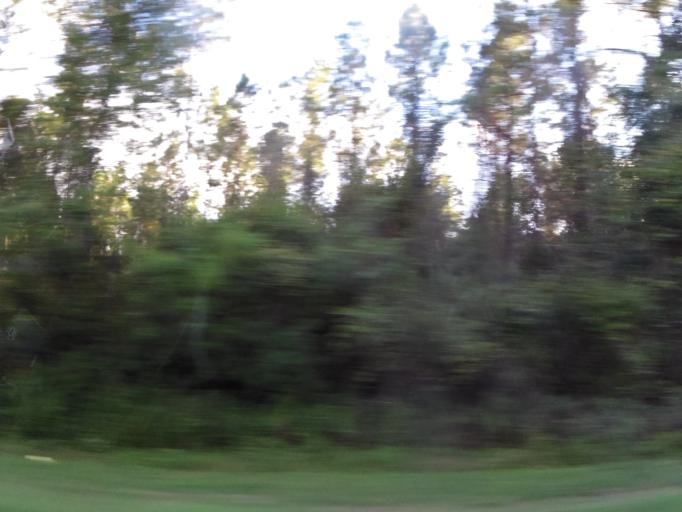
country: US
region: Georgia
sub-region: Lowndes County
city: Valdosta
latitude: 30.7926
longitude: -83.1822
